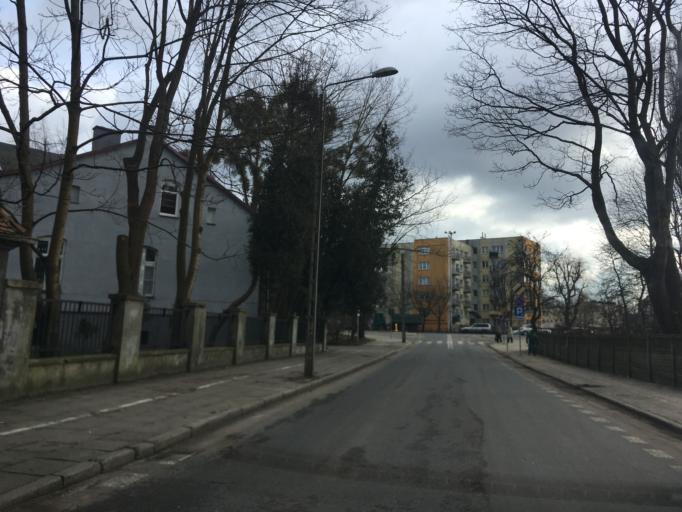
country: PL
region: Pomeranian Voivodeship
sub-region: Slupsk
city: Slupsk
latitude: 54.4657
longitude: 17.0365
